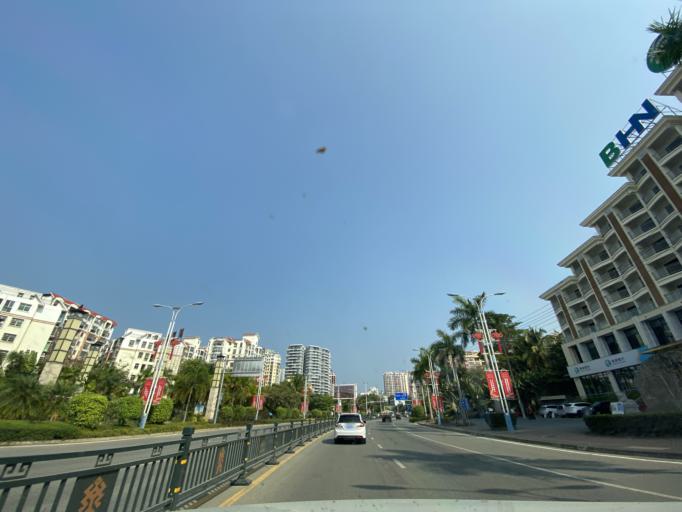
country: CN
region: Hainan
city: Chongshan
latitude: 18.7657
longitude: 109.5213
